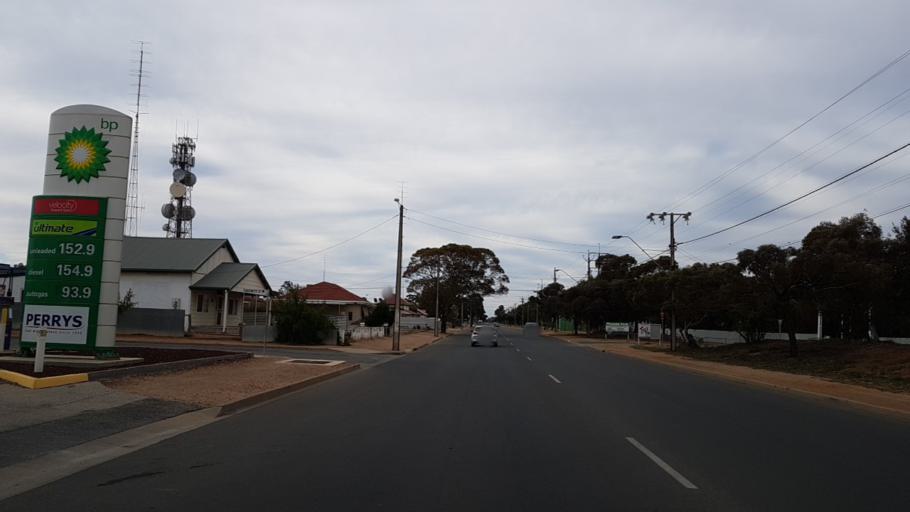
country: AU
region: South Australia
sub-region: Port Pirie City and Dists
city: Port Pirie
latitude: -33.1876
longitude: 138.0038
